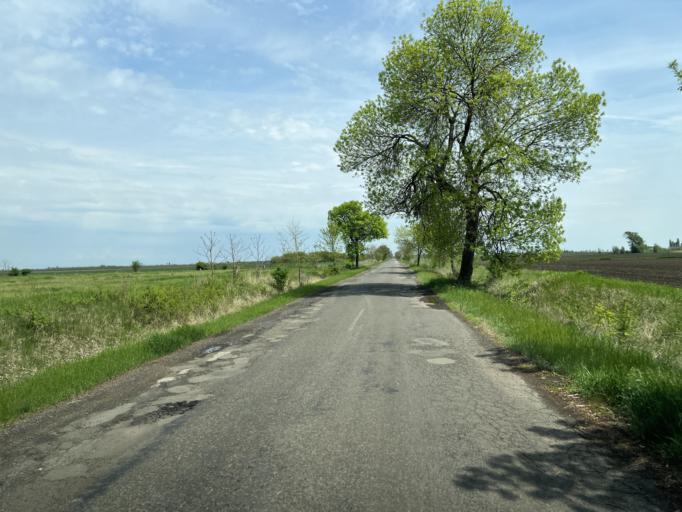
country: HU
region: Pest
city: Tapiogyorgye
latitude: 47.3497
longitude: 19.9552
